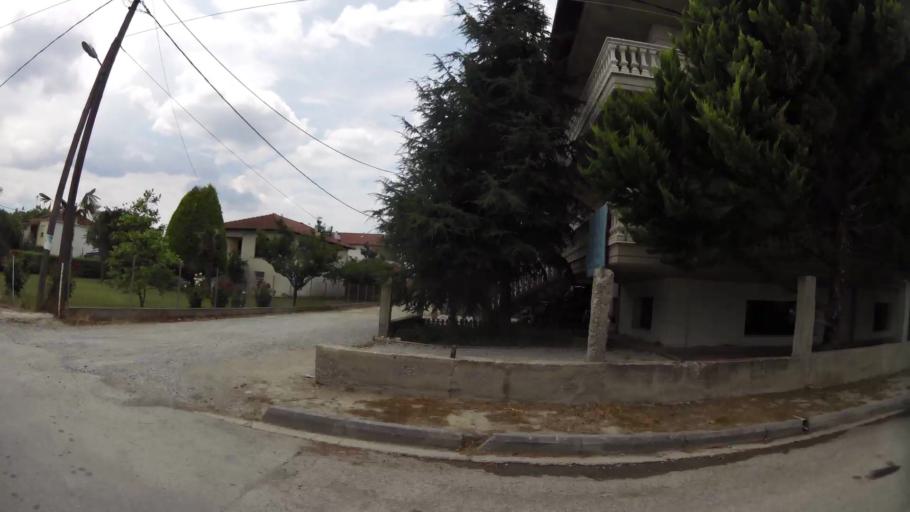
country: GR
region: Central Macedonia
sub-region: Nomos Pierias
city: Kallithea
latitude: 40.2759
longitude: 22.5747
